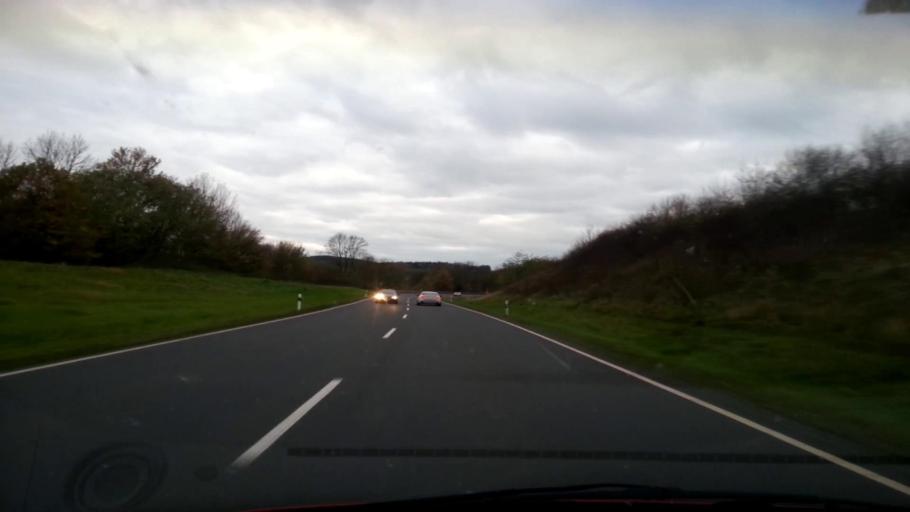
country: DE
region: Bavaria
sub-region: Upper Franconia
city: Schneckenlohe
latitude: 50.2137
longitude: 11.2175
